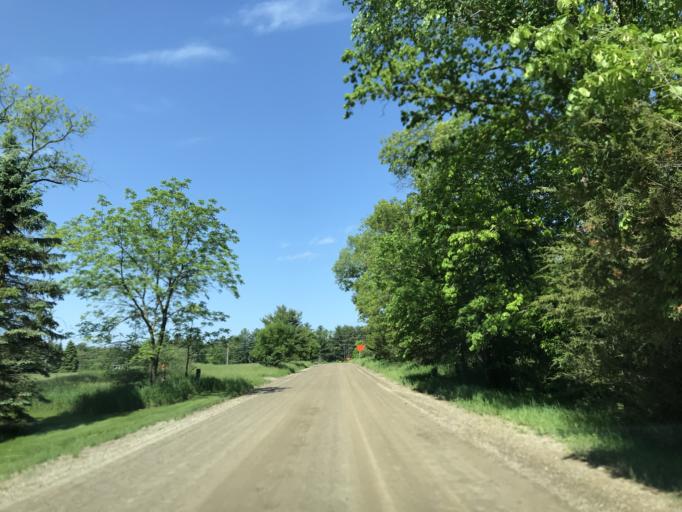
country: US
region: Michigan
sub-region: Oakland County
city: South Lyon
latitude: 42.4810
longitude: -83.6938
